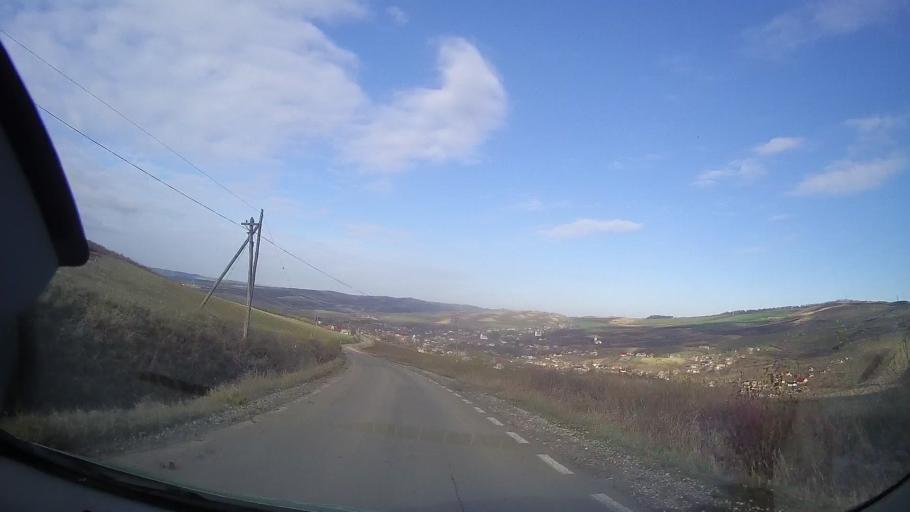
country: RO
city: Barza
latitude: 46.5471
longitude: 24.1471
